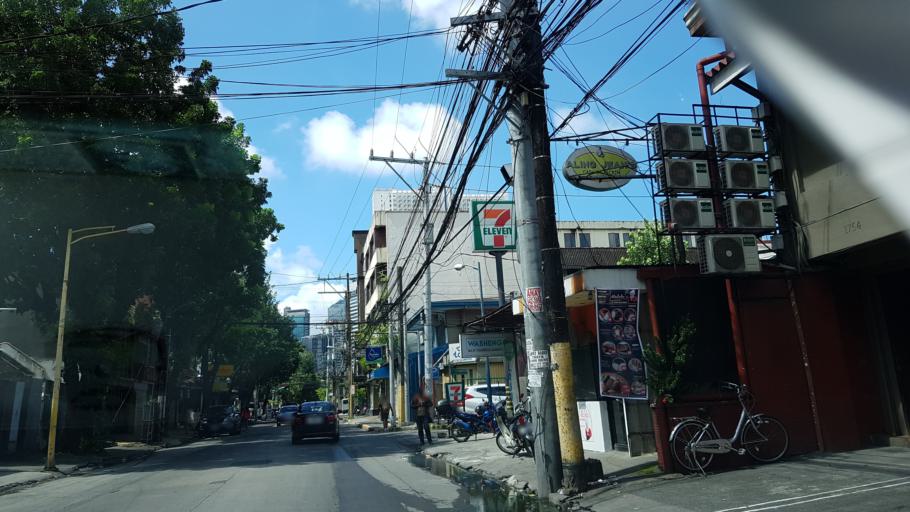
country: PH
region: Metro Manila
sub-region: Makati City
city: Makati City
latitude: 14.5681
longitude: 121.0240
